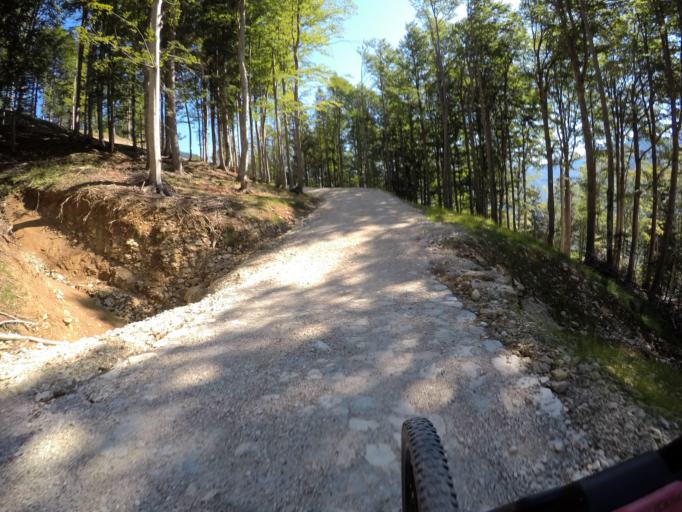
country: IT
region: Friuli Venezia Giulia
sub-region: Provincia di Udine
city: Malborghetto
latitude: 46.4569
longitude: 13.4564
